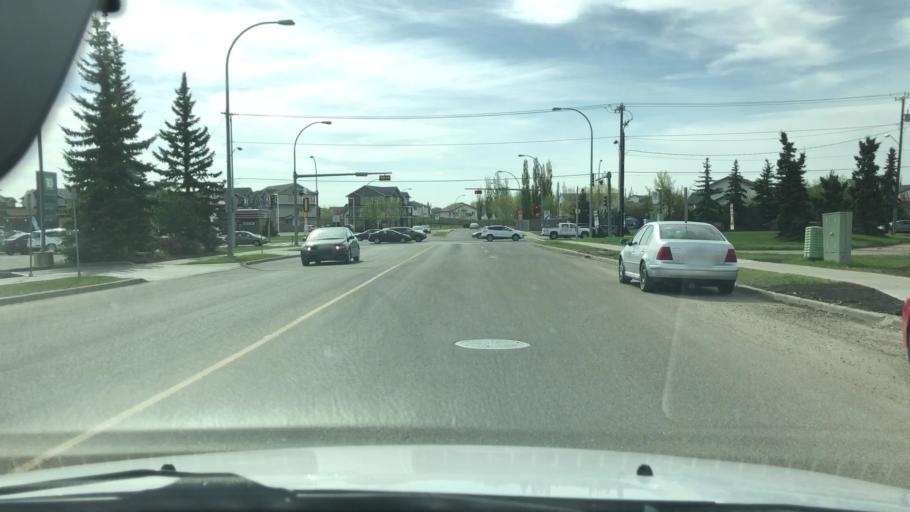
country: CA
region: Alberta
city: Edmonton
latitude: 53.6042
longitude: -113.5399
